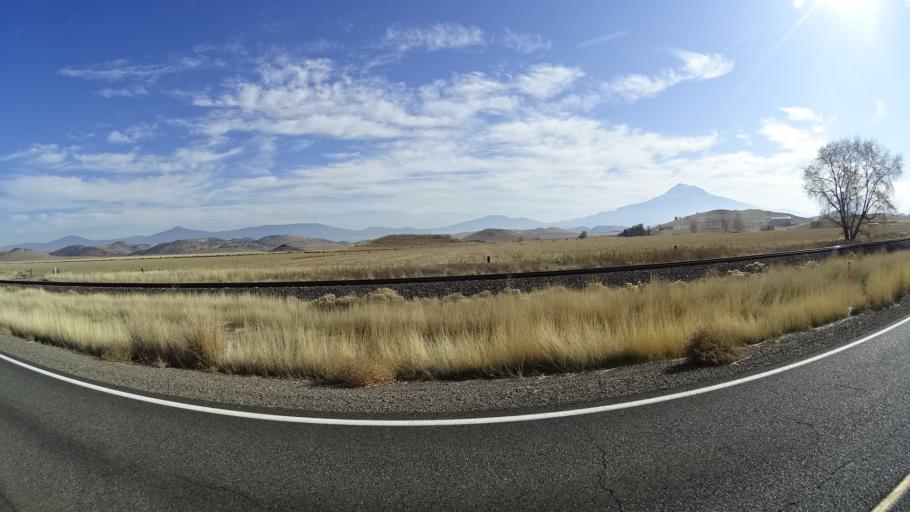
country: US
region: California
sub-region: Siskiyou County
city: Montague
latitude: 41.5669
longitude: -122.5255
